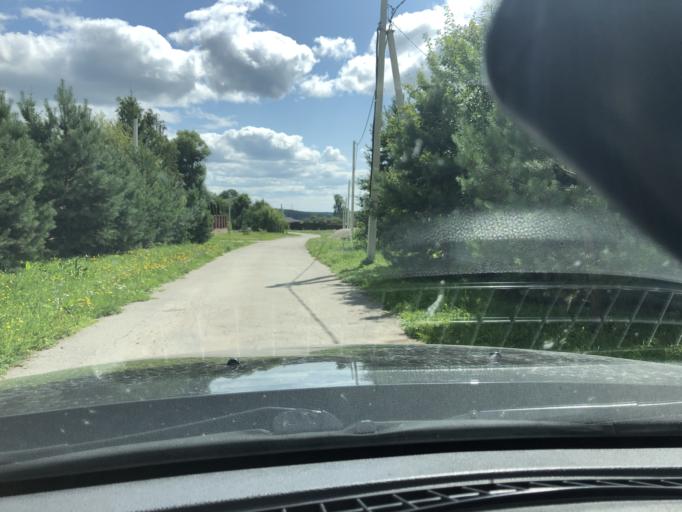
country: RU
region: Tula
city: Revyakino
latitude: 54.3502
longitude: 37.6154
